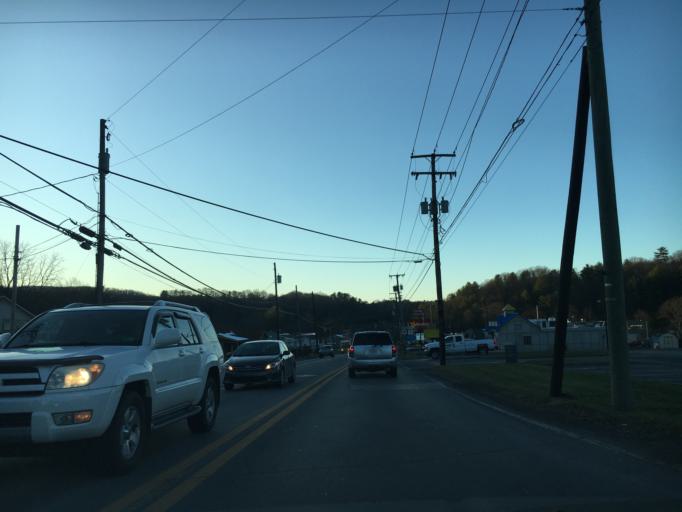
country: US
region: West Virginia
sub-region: Raleigh County
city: Beaver
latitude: 37.7490
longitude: -81.1349
